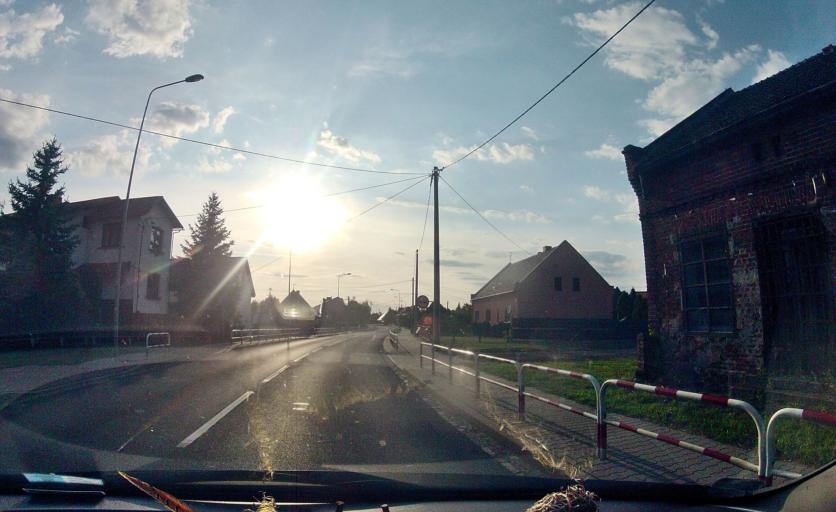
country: PL
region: Opole Voivodeship
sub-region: Powiat kluczborski
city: Kluczbork
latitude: 50.9743
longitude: 18.2361
